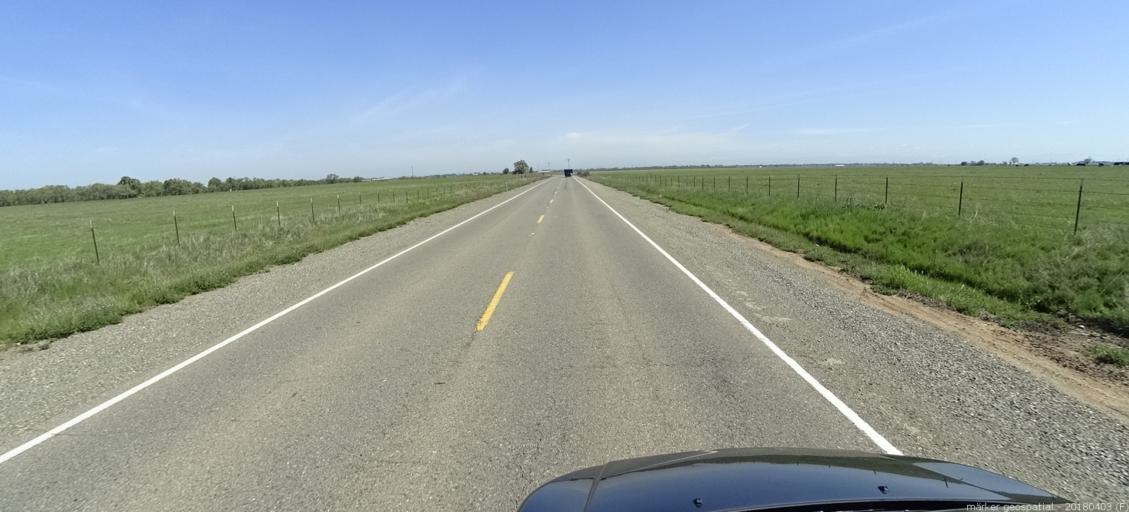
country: US
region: California
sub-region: Sacramento County
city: Wilton
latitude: 38.3613
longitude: -121.3117
